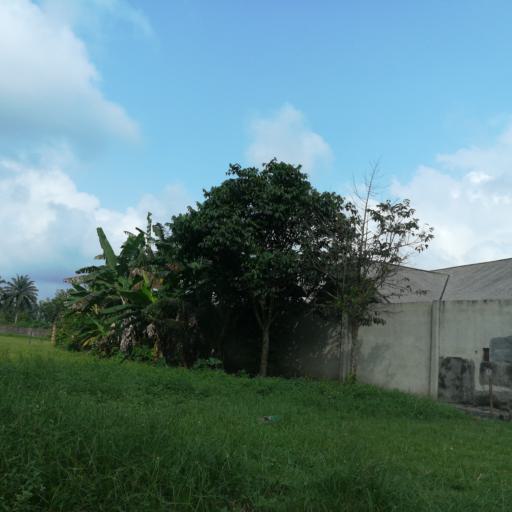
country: NG
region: Rivers
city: Okrika
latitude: 4.7810
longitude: 7.1380
